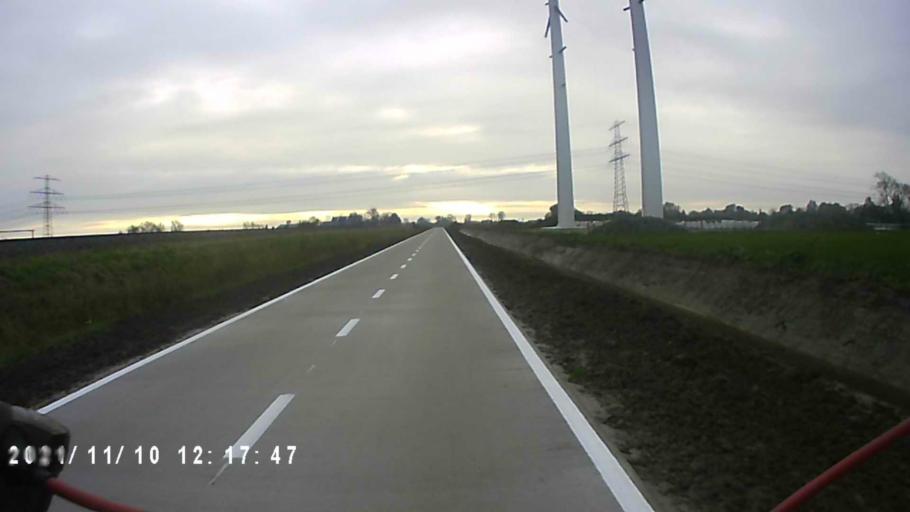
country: NL
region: Groningen
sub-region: Gemeente Winsum
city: Winsum
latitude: 53.3024
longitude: 6.5384
